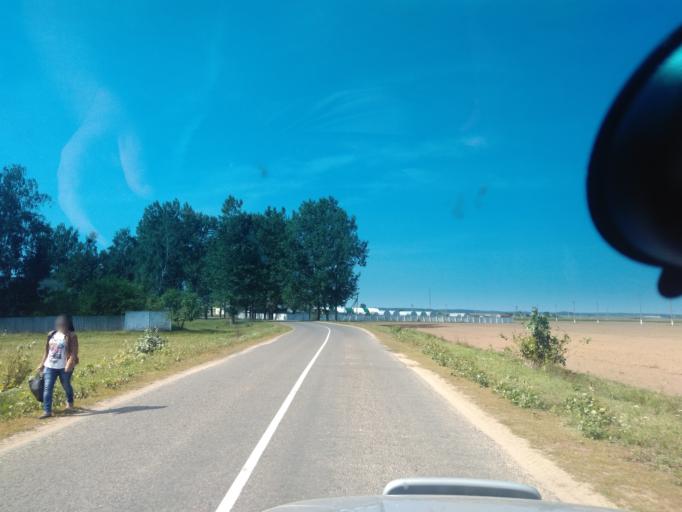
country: BY
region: Minsk
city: Kapyl'
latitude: 53.2592
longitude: 27.1850
